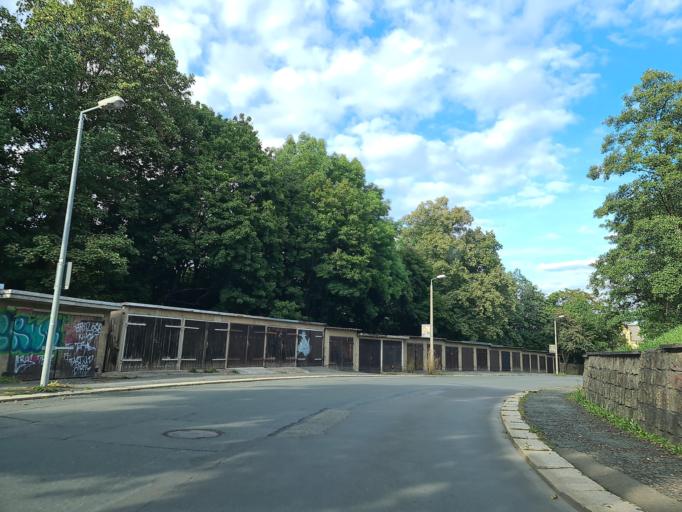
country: DE
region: Saxony
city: Plauen
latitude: 50.4884
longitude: 12.1420
